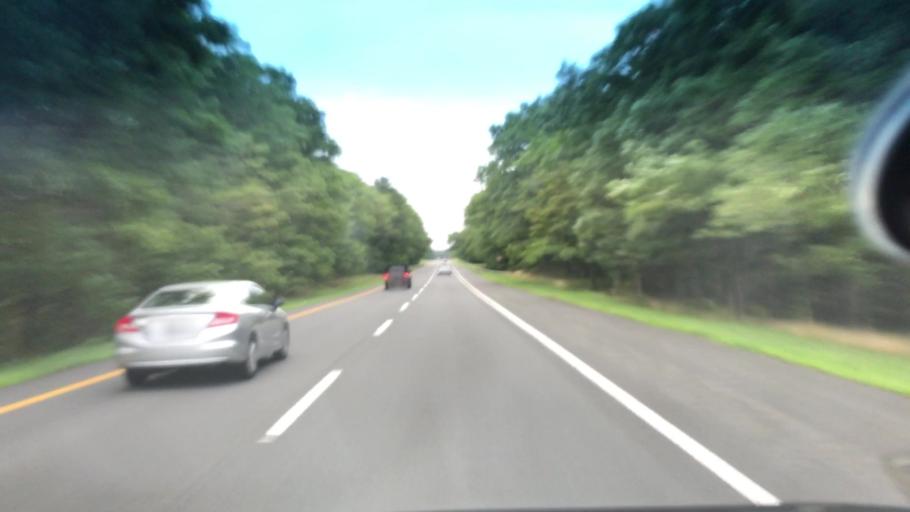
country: US
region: New York
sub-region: Suffolk County
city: East Shoreham
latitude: 40.9302
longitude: -72.8791
